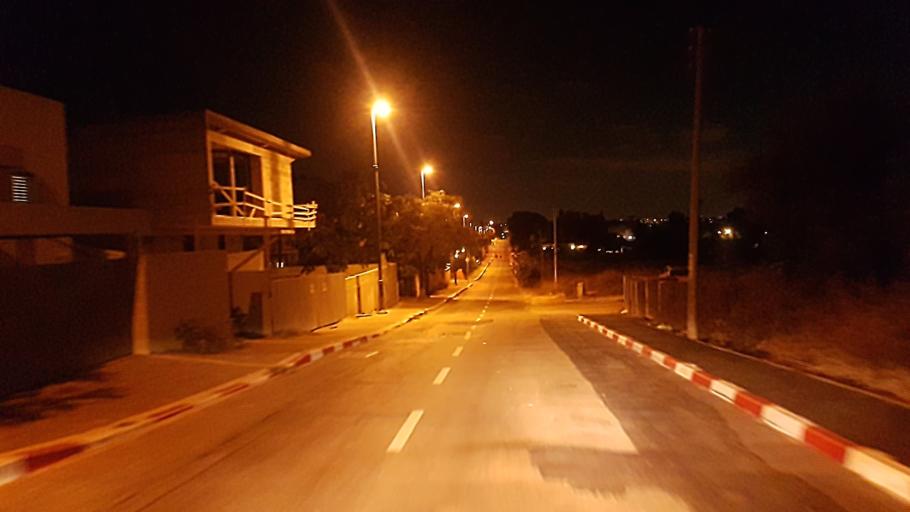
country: IL
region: Central District
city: Hod HaSharon
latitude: 32.1668
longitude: 34.8898
